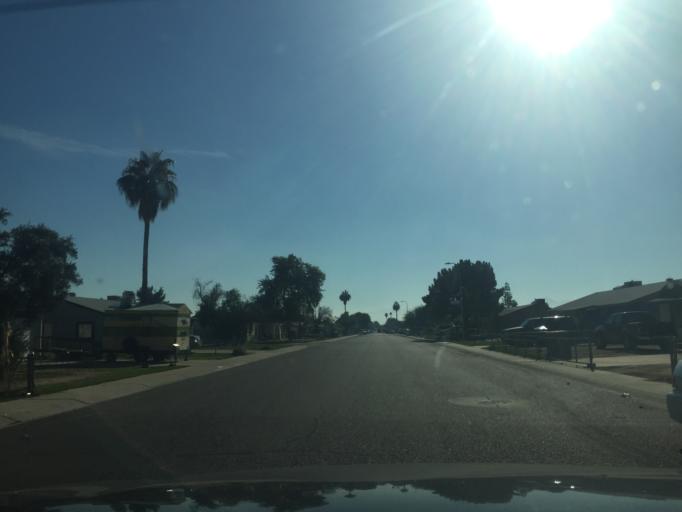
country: US
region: Arizona
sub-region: Maricopa County
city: Tolleson
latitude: 33.4718
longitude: -112.2164
